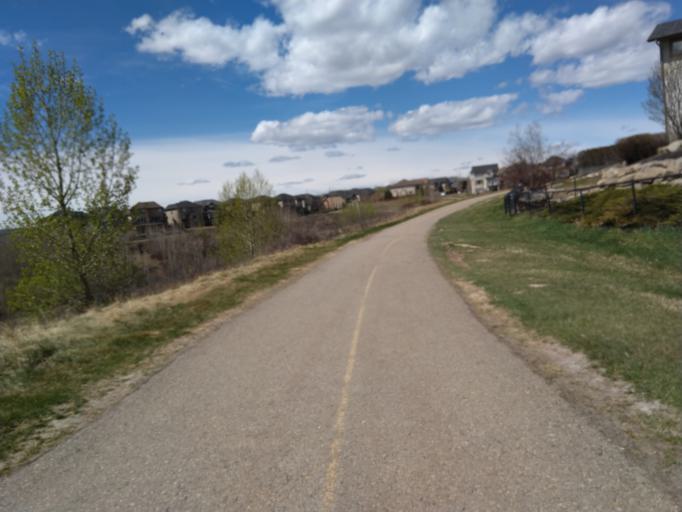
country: CA
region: Alberta
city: Calgary
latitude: 51.1120
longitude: -114.2434
